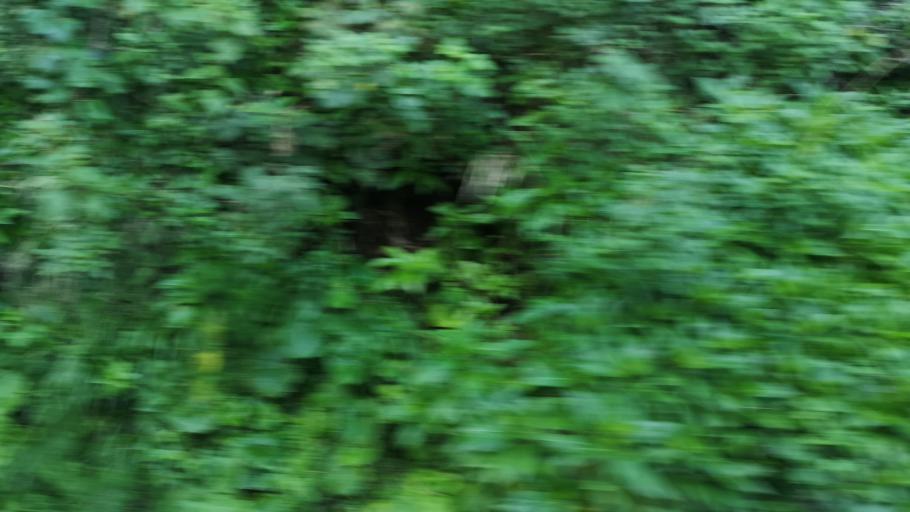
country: ES
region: Canary Islands
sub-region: Provincia de Santa Cruz de Tenerife
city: Hermigua
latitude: 28.1326
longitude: -17.2014
